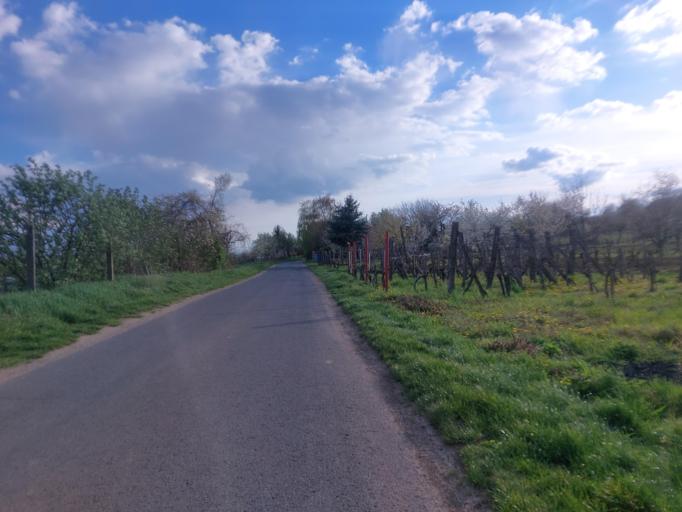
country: HU
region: Veszprem
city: Devecser
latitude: 47.1400
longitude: 17.3867
